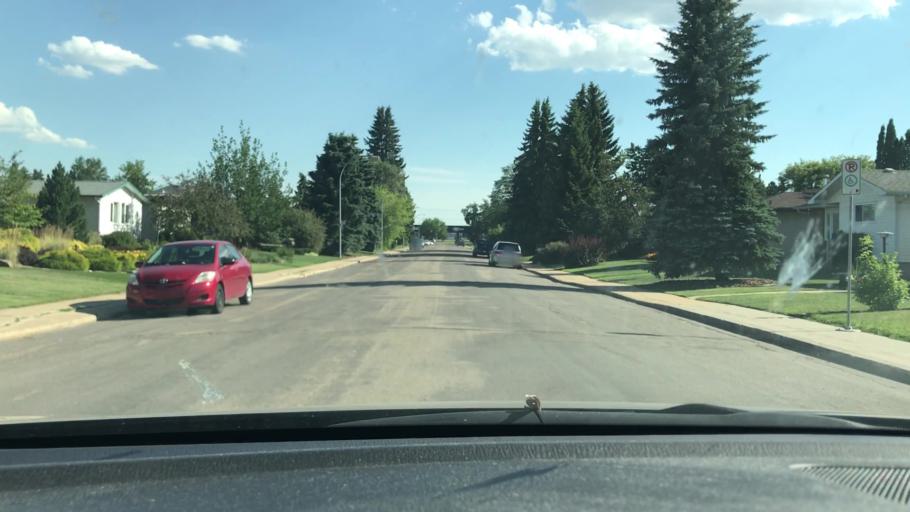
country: CA
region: Alberta
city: Edmonton
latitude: 53.5213
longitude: -113.4229
